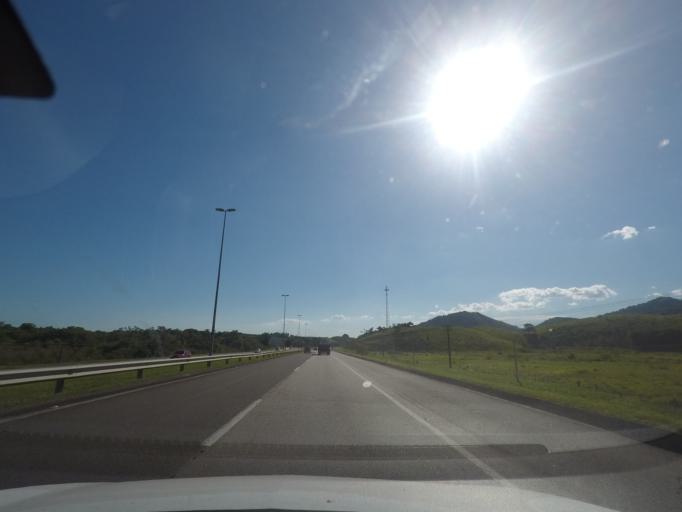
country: BR
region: Rio de Janeiro
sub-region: Guapimirim
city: Guapimirim
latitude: -22.6493
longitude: -43.0747
